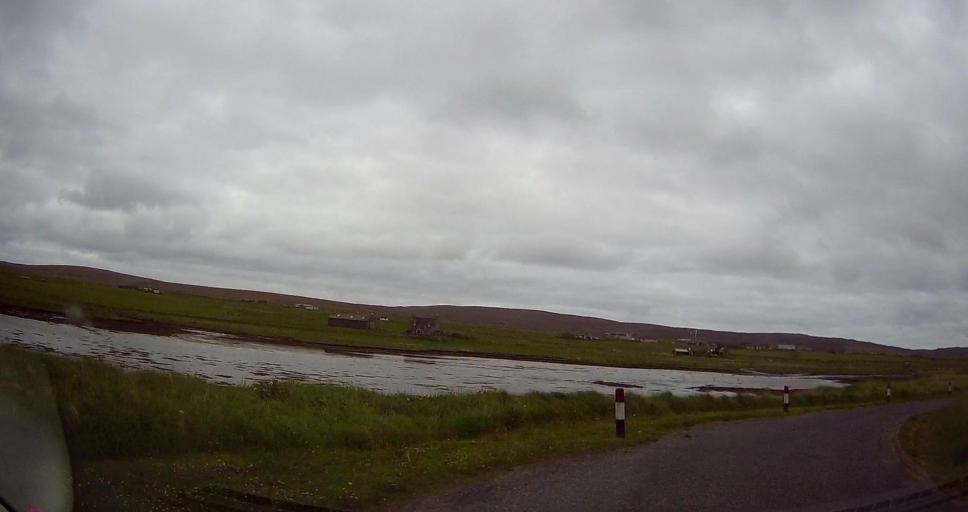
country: GB
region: Scotland
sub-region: Shetland Islands
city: Shetland
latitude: 60.7572
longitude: -0.8611
